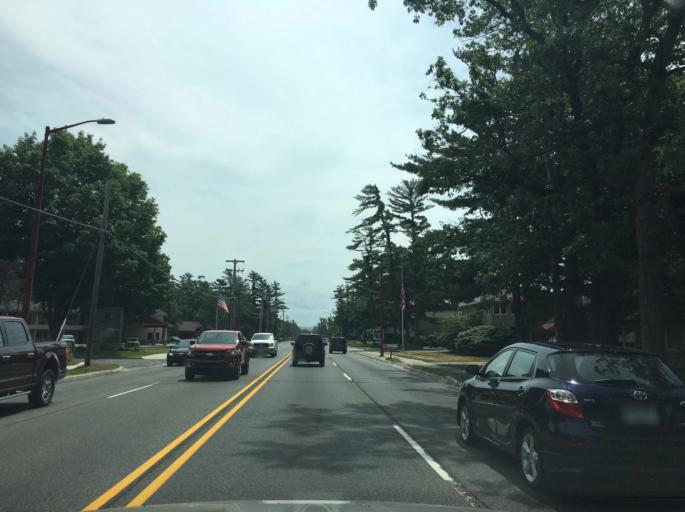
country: US
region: Michigan
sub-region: Grand Traverse County
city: Traverse City
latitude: 44.7613
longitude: -85.5836
